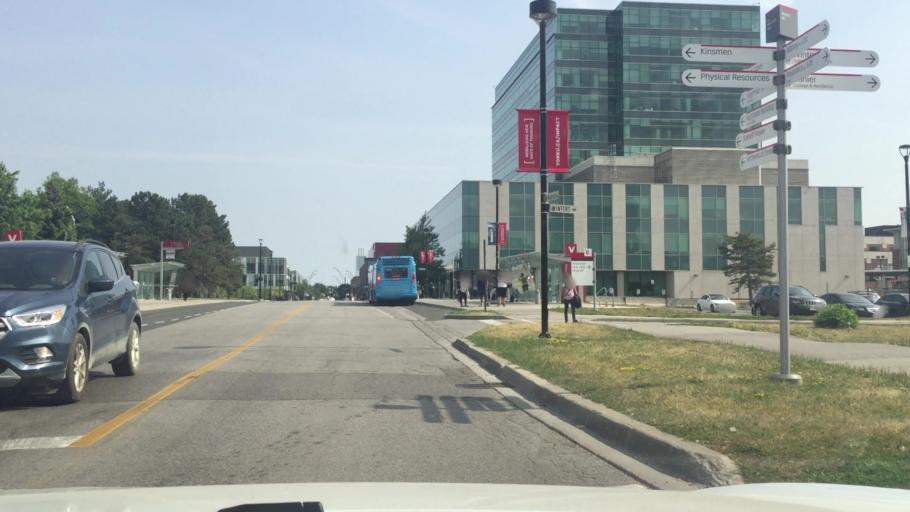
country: CA
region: Ontario
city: Concord
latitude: 43.7763
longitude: -79.5007
